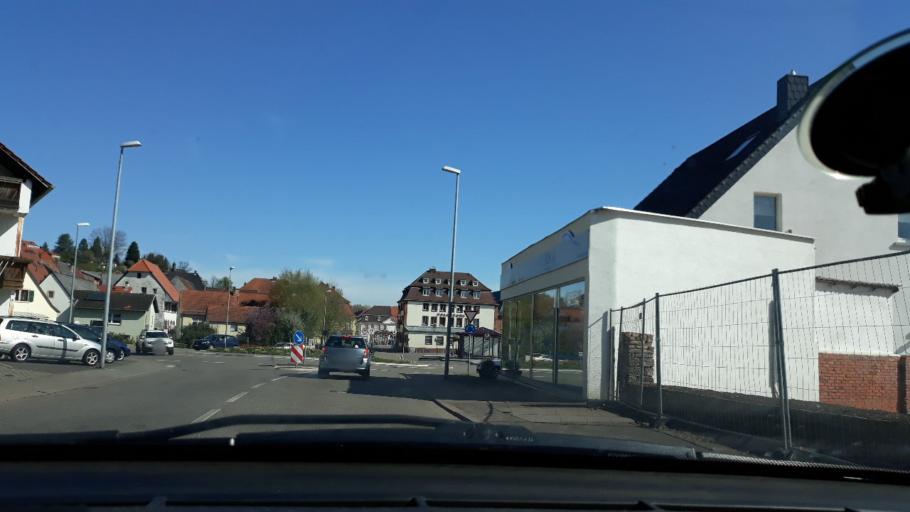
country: DE
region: Saarland
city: Blieskastel
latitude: 49.2354
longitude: 7.2586
